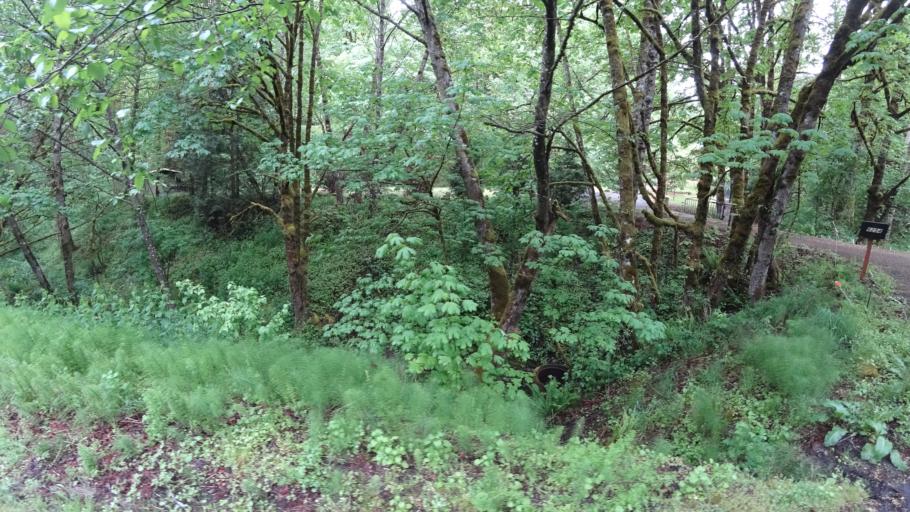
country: US
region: Oregon
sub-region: Washington County
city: West Haven-Sylvan
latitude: 45.5345
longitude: -122.7408
